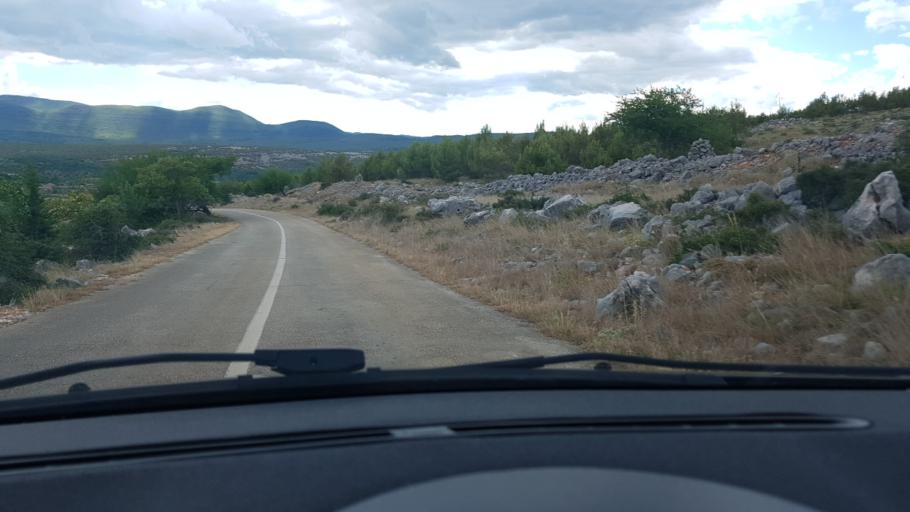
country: HR
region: Zadarska
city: Gracac
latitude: 44.1656
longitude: 15.8707
